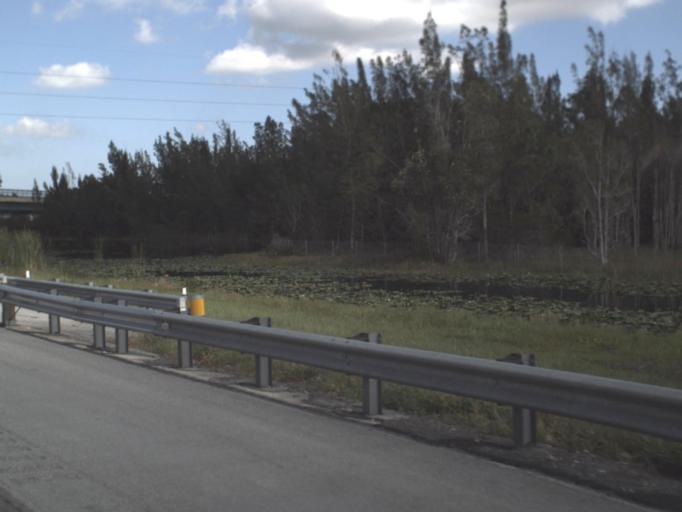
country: US
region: Florida
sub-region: Palm Beach County
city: Schall Circle
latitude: 26.7580
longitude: -80.1340
